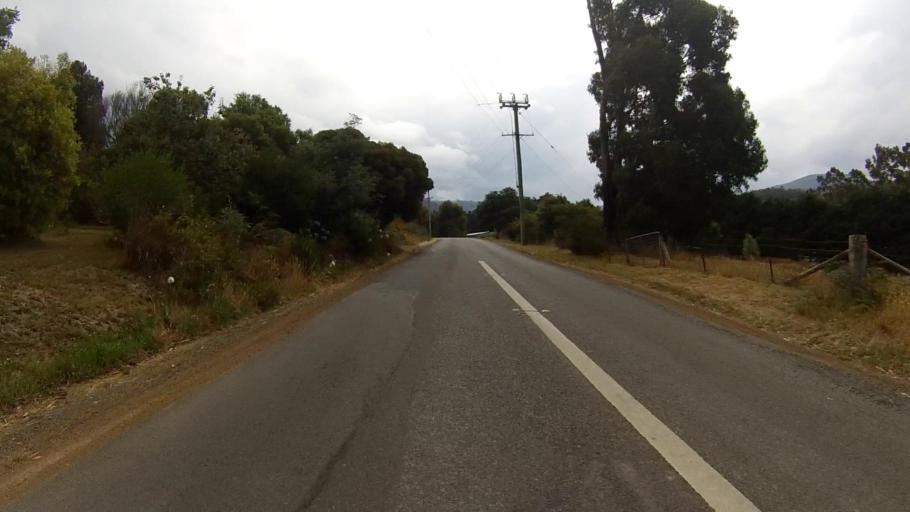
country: AU
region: Tasmania
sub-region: Huon Valley
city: Huonville
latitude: -42.9811
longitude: 147.0544
